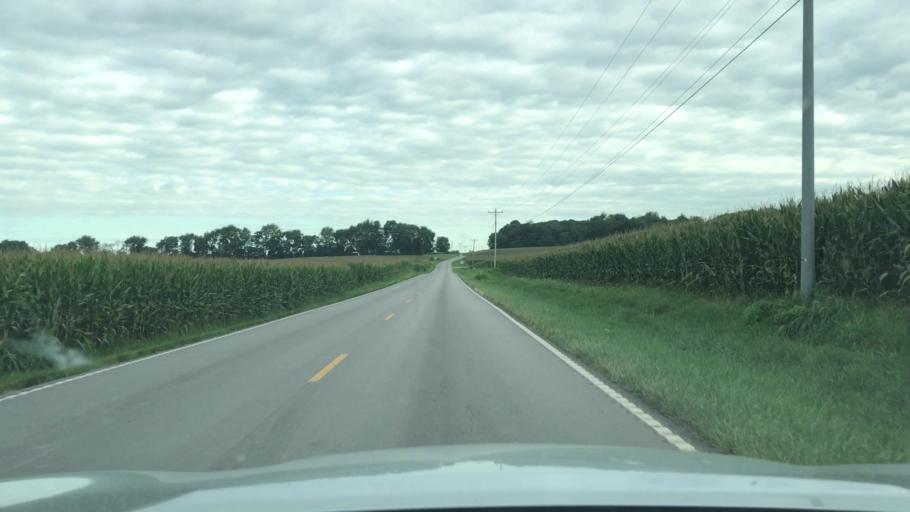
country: US
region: Kentucky
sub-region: Todd County
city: Guthrie
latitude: 36.6797
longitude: -87.1997
